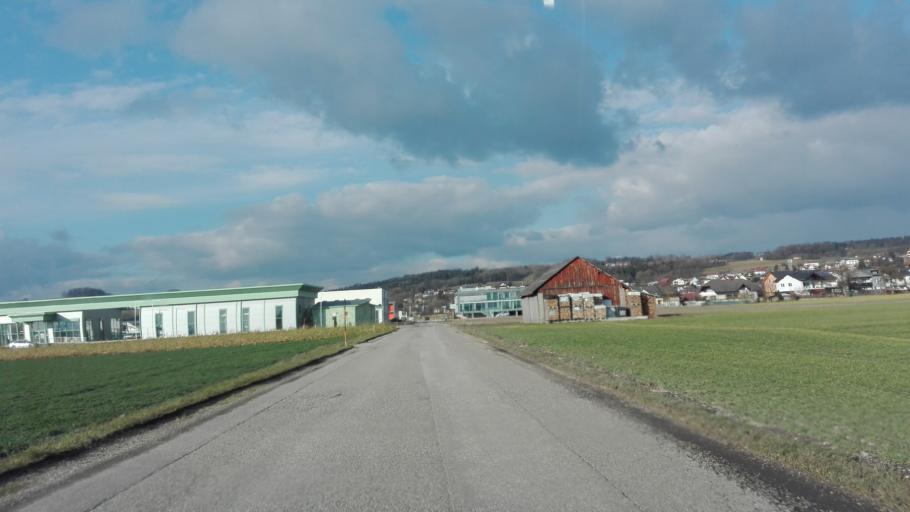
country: AT
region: Upper Austria
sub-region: Politischer Bezirk Perg
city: Perg
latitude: 48.2431
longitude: 14.6200
